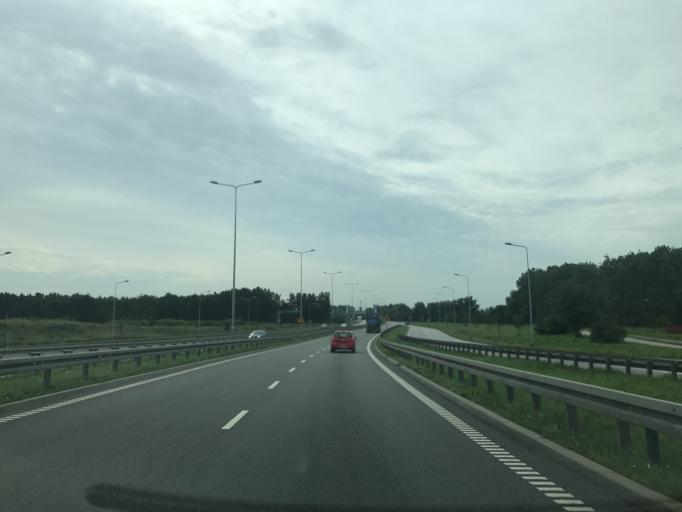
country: PL
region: Pomeranian Voivodeship
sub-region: Gdansk
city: Gdansk
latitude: 54.3753
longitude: 18.6832
